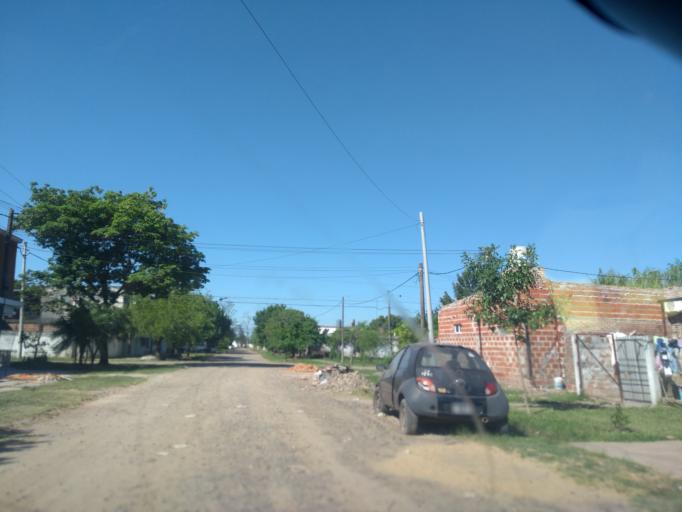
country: AR
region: Chaco
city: Resistencia
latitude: -27.4731
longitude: -58.9801
